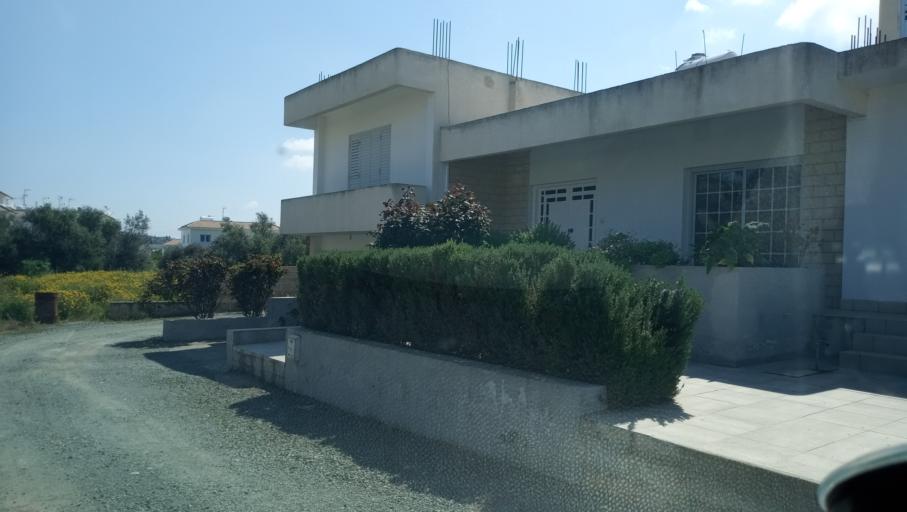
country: CY
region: Lefkosia
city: Alampra
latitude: 35.0115
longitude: 33.4005
